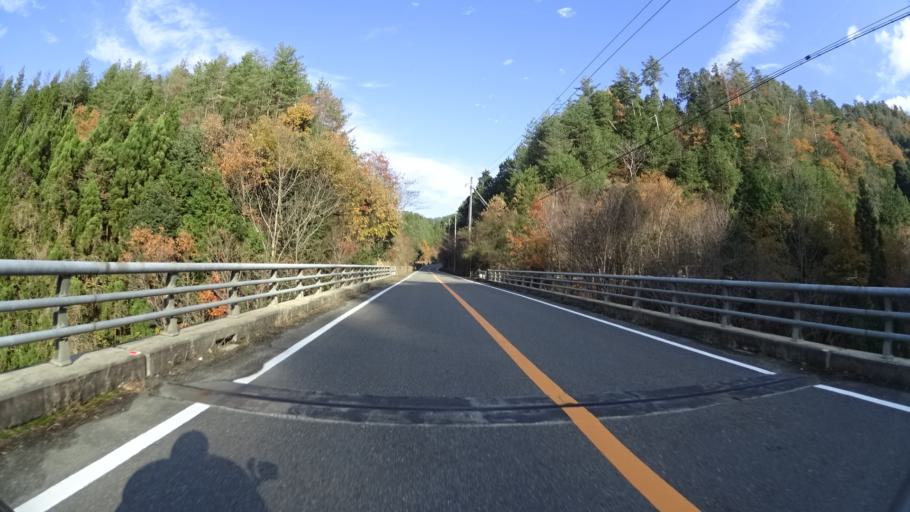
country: JP
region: Kyoto
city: Kameoka
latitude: 35.1298
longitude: 135.5462
